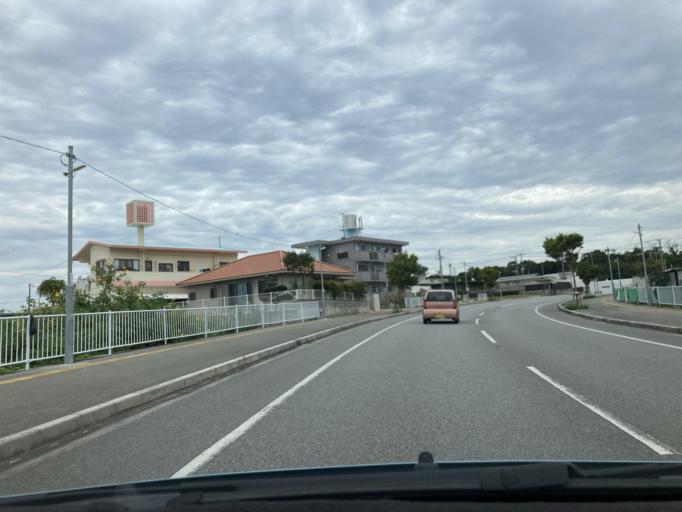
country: JP
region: Okinawa
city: Ishikawa
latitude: 26.4012
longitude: 127.7391
